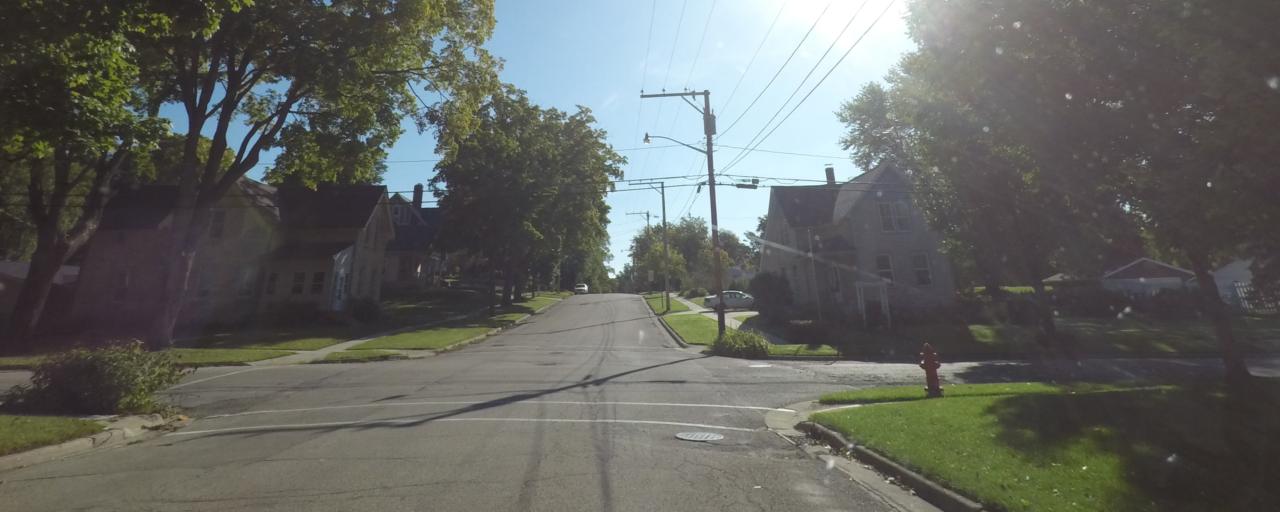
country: US
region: Wisconsin
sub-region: Jefferson County
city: Jefferson
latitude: 43.0079
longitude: -88.8037
